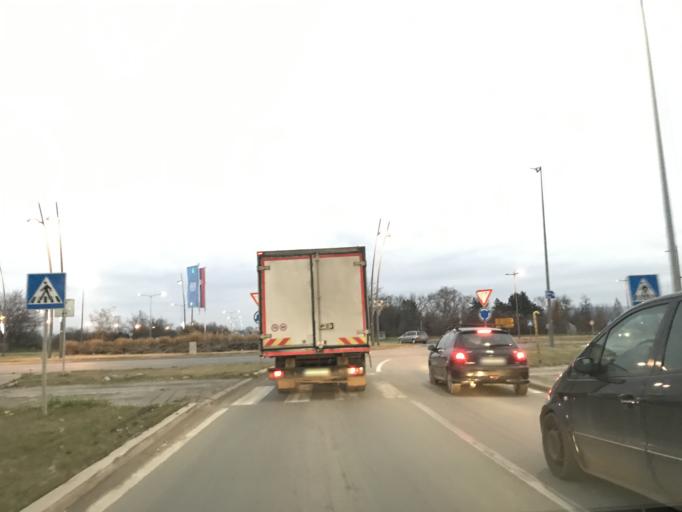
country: RS
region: Autonomna Pokrajina Vojvodina
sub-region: Juznobacki Okrug
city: Novi Sad
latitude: 45.2752
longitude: 19.8011
